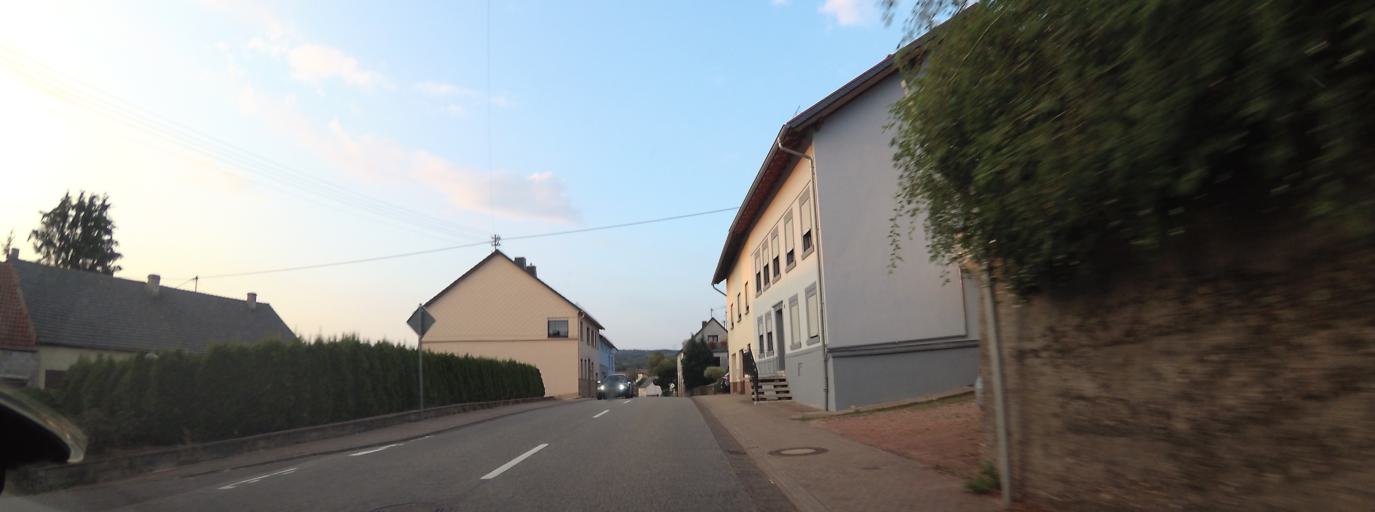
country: DE
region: Saarland
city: Tholey
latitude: 49.5325
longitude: 6.9749
